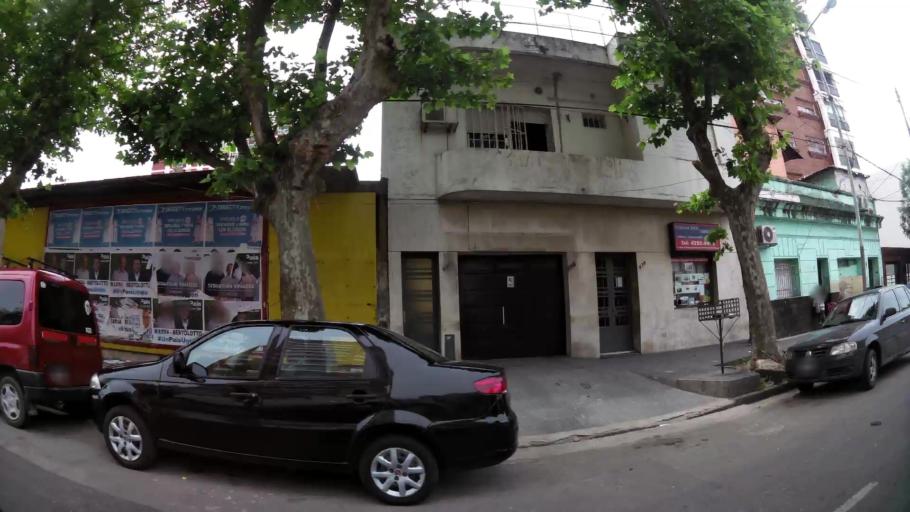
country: AR
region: Buenos Aires
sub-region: Partido de Avellaneda
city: Avellaneda
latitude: -34.6628
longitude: -58.3700
